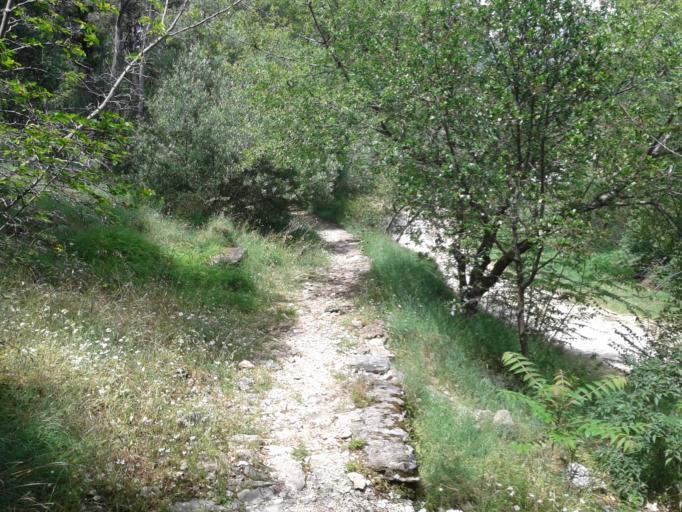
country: HR
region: Splitsko-Dalmatinska
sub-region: Grad Split
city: Split
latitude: 43.5112
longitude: 16.4205
